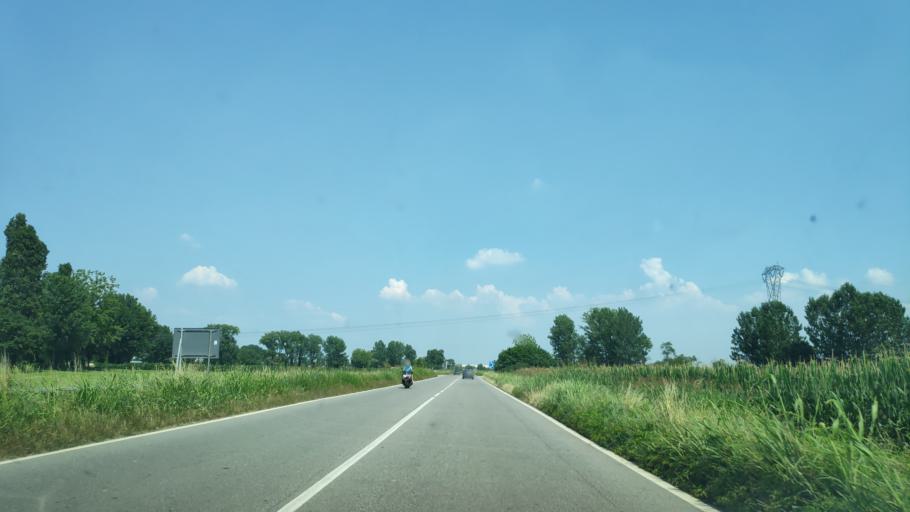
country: IT
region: Lombardy
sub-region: Citta metropolitana di Milano
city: Liscate
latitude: 45.4838
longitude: 9.3964
